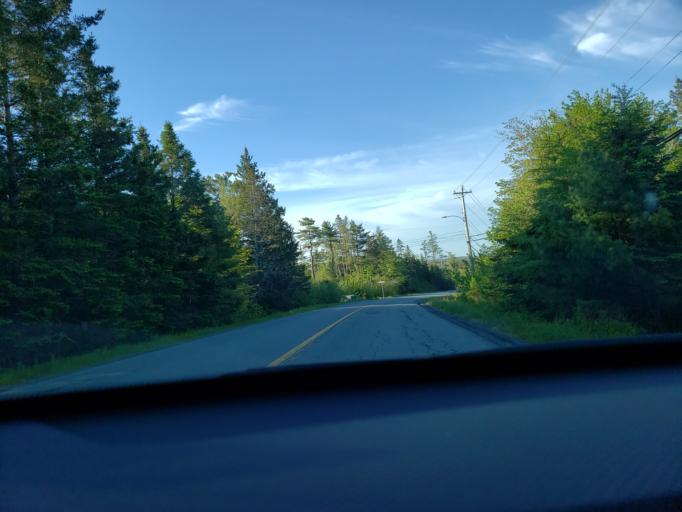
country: CA
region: Nova Scotia
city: Cole Harbour
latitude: 44.7185
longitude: -63.3972
